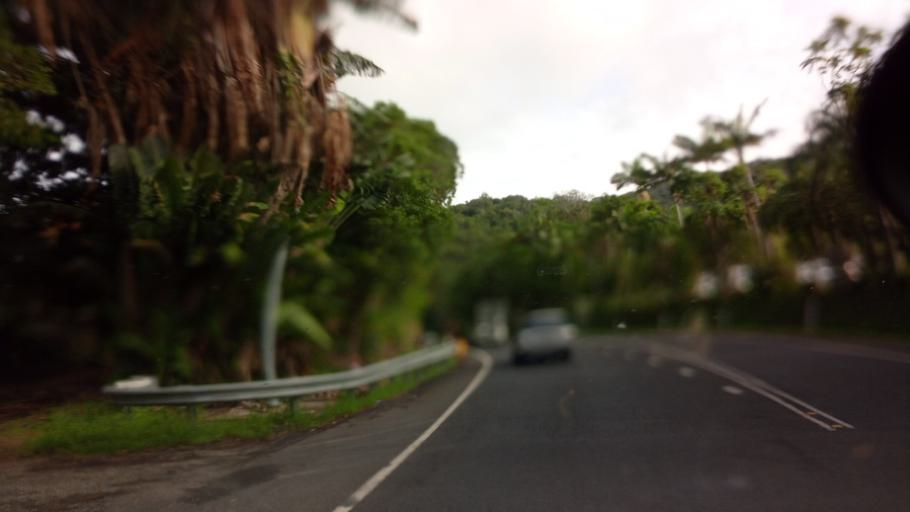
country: AU
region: Queensland
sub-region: Tablelands
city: Kuranda
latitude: -16.8254
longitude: 145.6511
